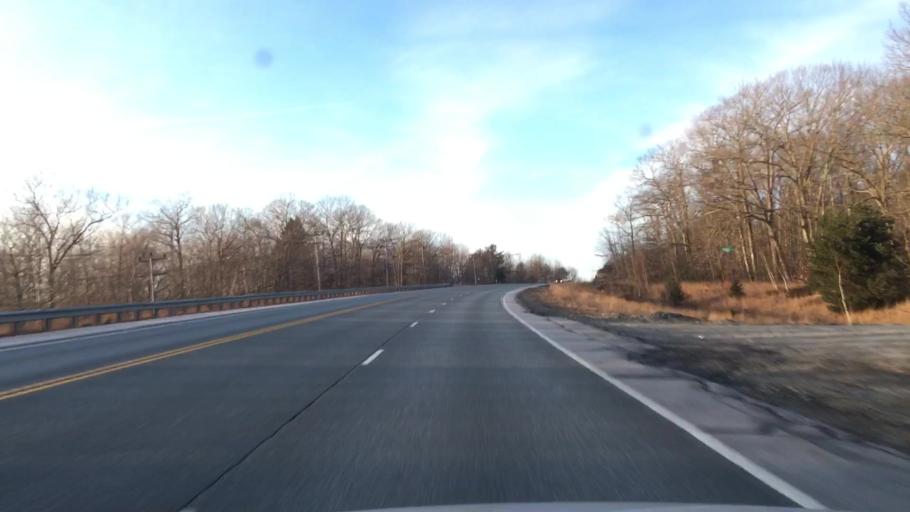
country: US
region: Maine
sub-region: Hancock County
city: Dedham
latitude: 44.6969
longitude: -68.5947
